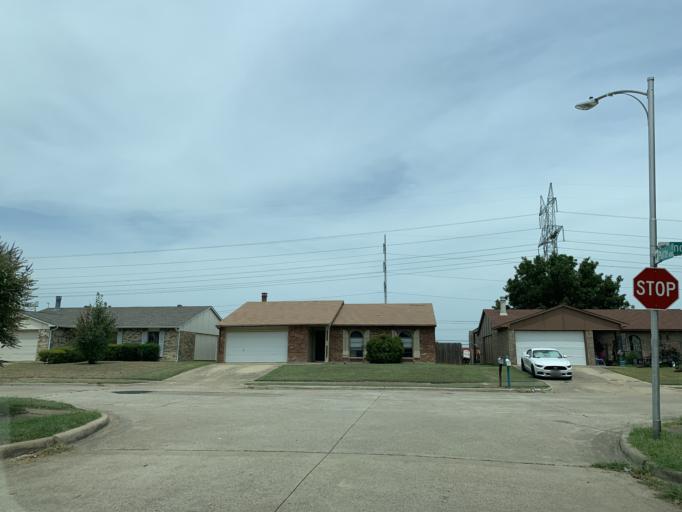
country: US
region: Texas
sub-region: Dallas County
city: Grand Prairie
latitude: 32.6564
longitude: -97.0248
